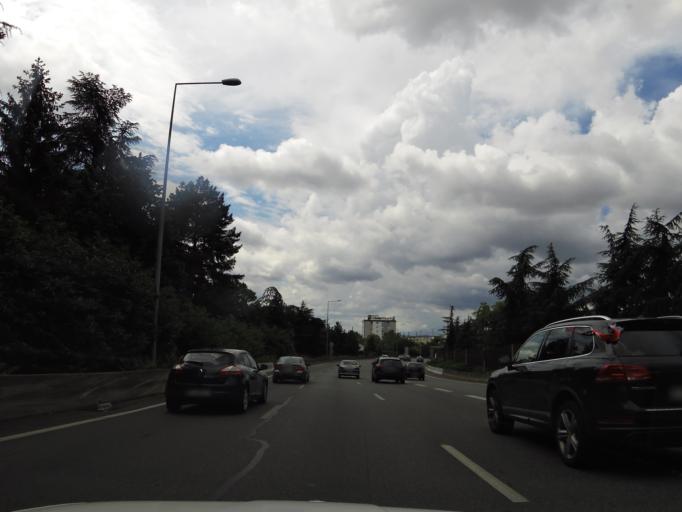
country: FR
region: Rhone-Alpes
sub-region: Departement du Rhone
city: Bron
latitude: 45.7255
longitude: 4.8930
